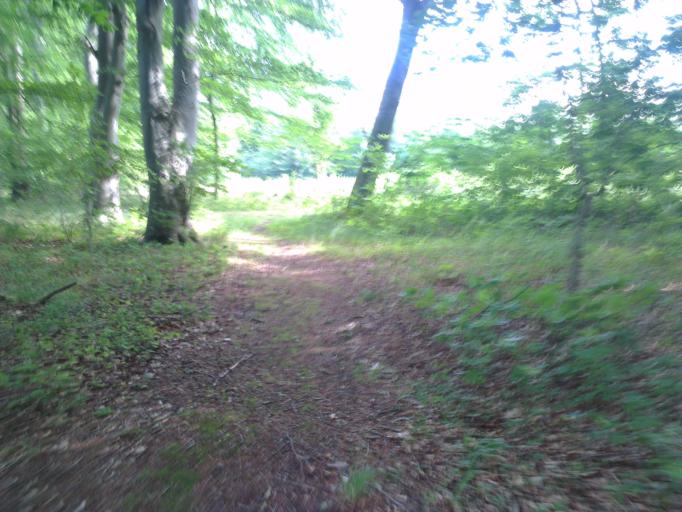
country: DK
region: Capital Region
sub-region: Frederikssund Kommune
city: Jaegerspris
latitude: 55.8844
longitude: 11.9807
